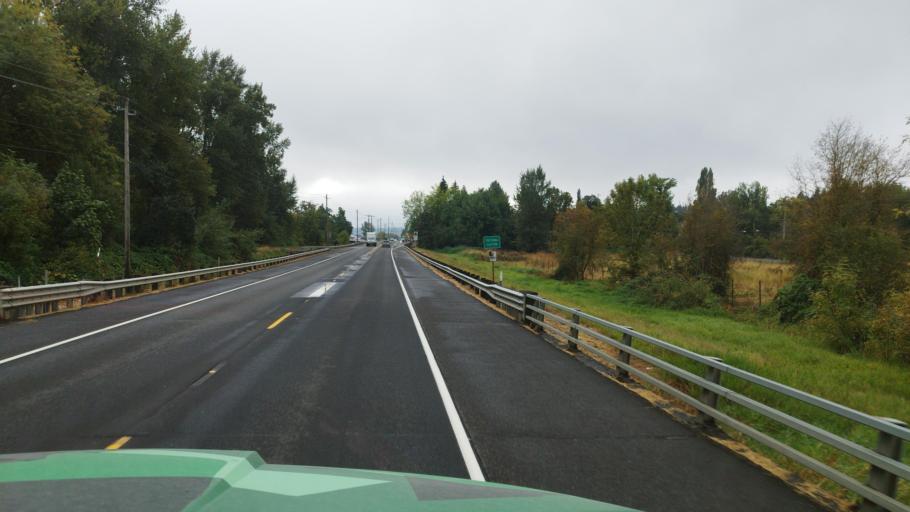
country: US
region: Oregon
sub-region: Washington County
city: Forest Grove
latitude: 45.4410
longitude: -123.1409
